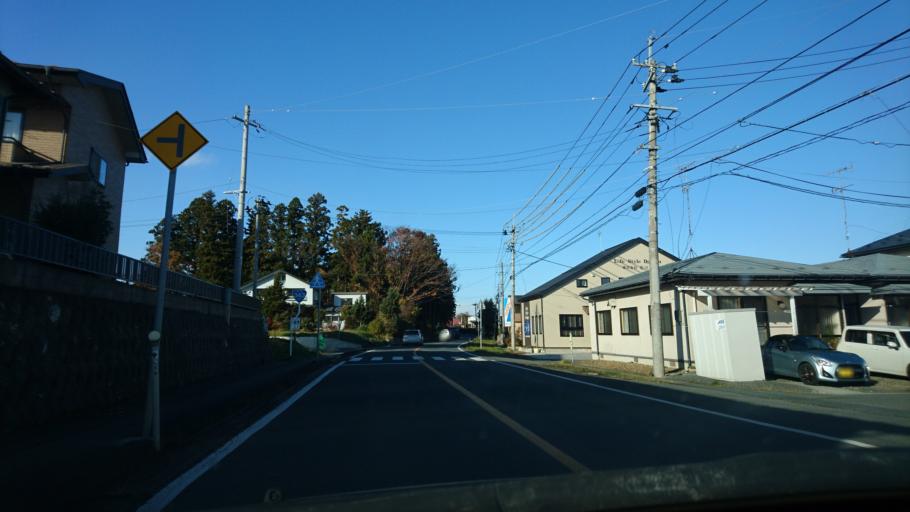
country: JP
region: Iwate
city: Mizusawa
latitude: 39.1202
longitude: 141.1648
